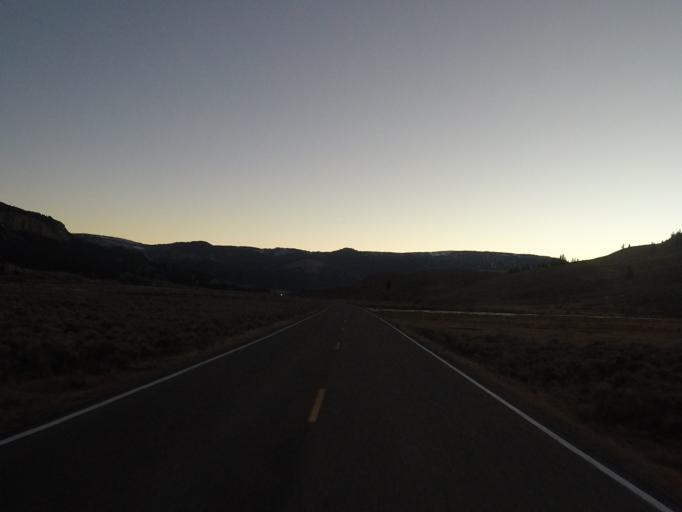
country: US
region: Montana
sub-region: Park County
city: Livingston
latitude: 44.8872
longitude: -110.1427
